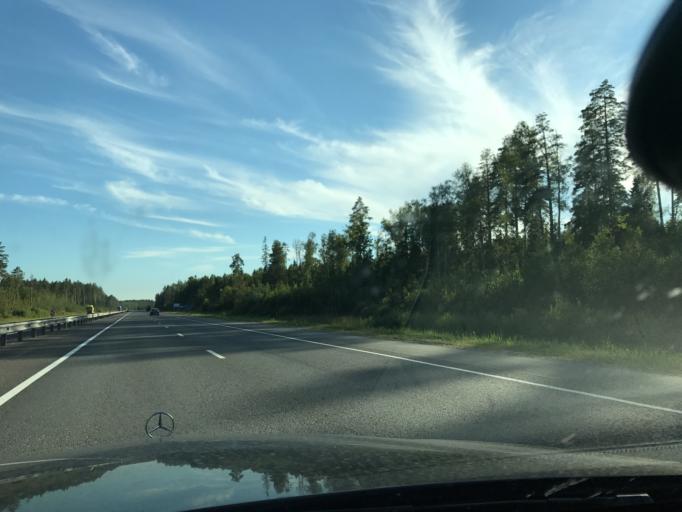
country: RU
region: Vladimir
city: Kameshkovo
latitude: 56.1592
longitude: 40.9270
